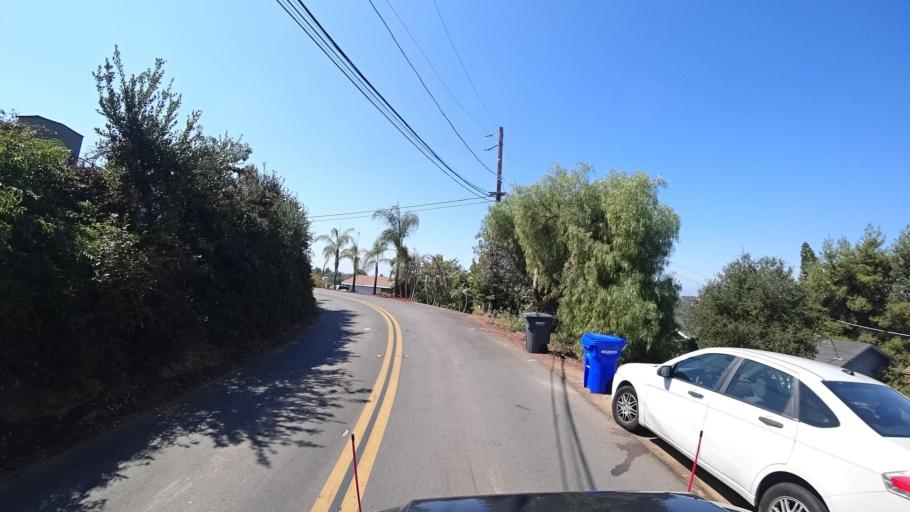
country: US
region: California
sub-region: San Diego County
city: Lake San Marcos
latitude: 33.1660
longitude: -117.2111
